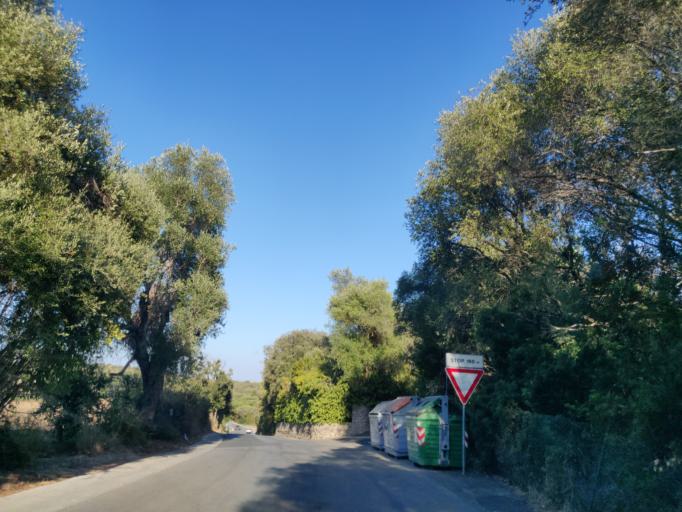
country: IT
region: Tuscany
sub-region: Provincia di Grosseto
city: Orbetello Scalo
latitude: 42.4119
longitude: 11.2948
